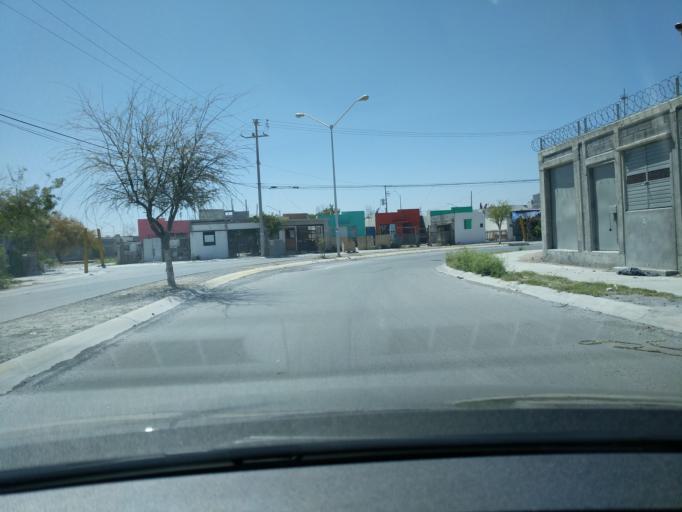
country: MX
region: Nuevo Leon
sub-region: Pesqueria
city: Colinas del Aeropuerto
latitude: 25.8245
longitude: -100.1175
